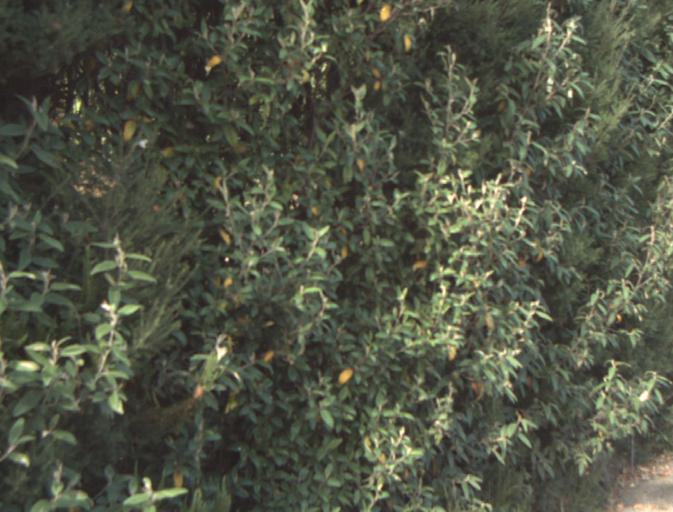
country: AU
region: Tasmania
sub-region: Launceston
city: Mayfield
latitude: -41.2613
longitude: 147.2546
